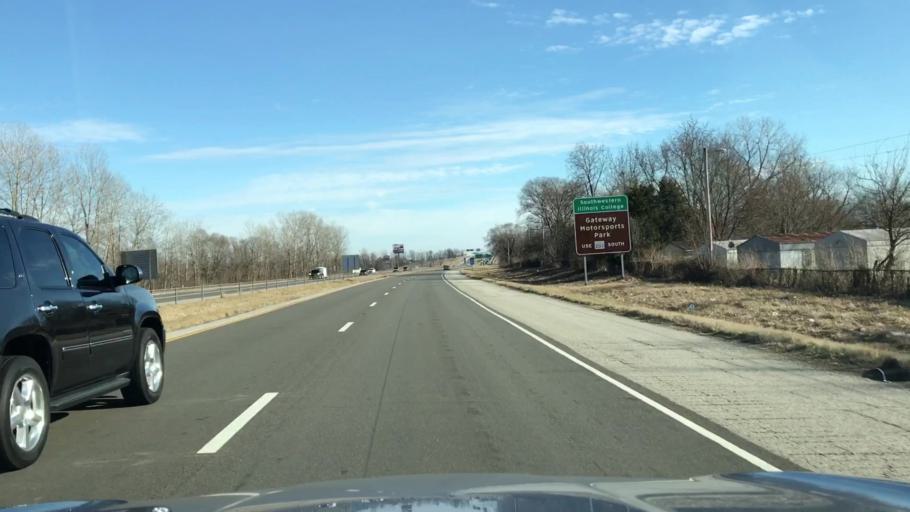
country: US
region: Illinois
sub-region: Madison County
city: Mitchell
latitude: 38.7644
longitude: -90.1084
